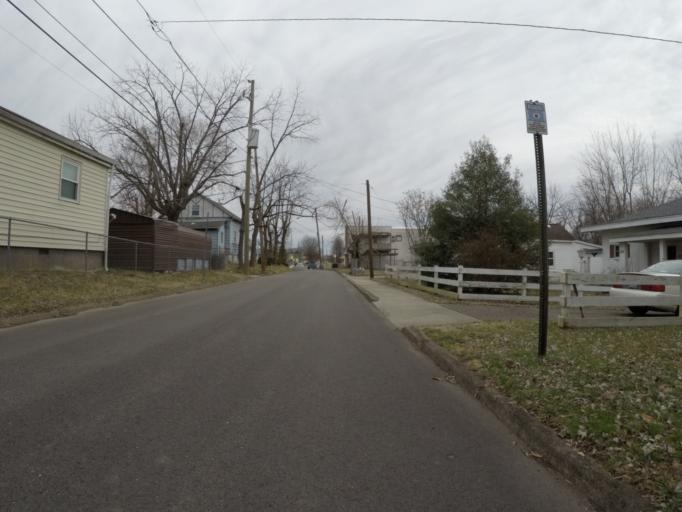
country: US
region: Ohio
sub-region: Lawrence County
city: Burlington
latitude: 38.4066
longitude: -82.4928
